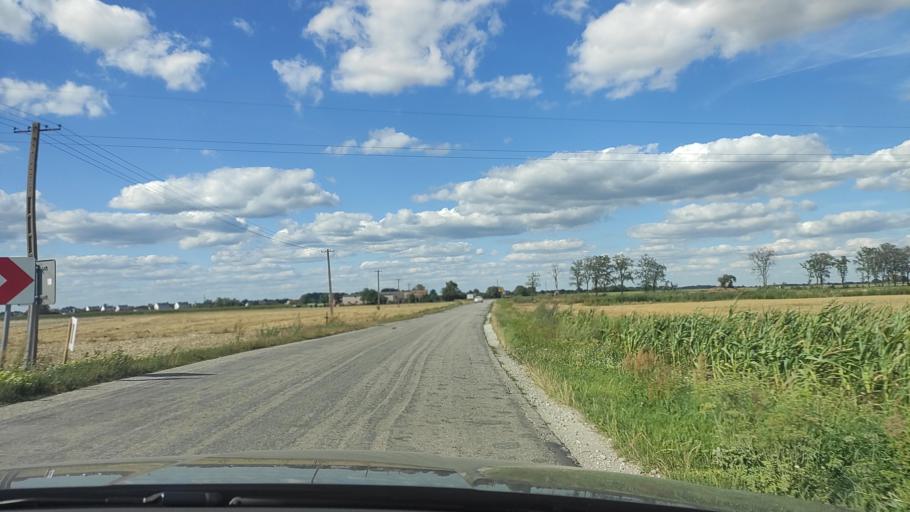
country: PL
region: Greater Poland Voivodeship
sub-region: Powiat poznanski
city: Kleszczewo
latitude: 52.3666
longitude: 17.1672
